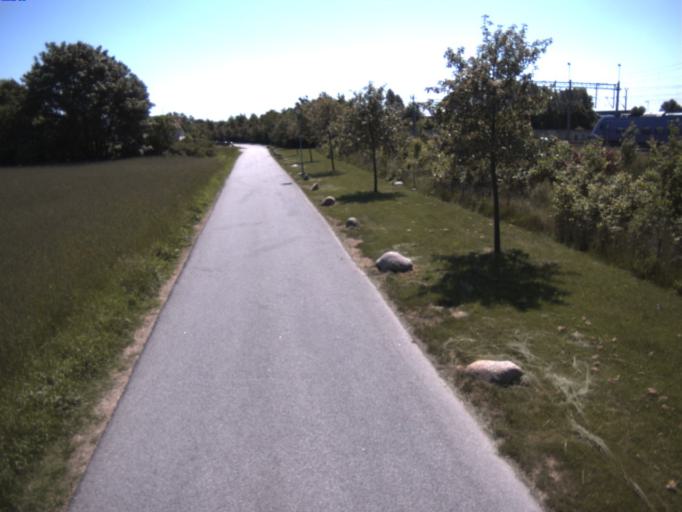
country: SE
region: Skane
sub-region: Helsingborg
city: Rydeback
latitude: 56.0051
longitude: 12.7468
